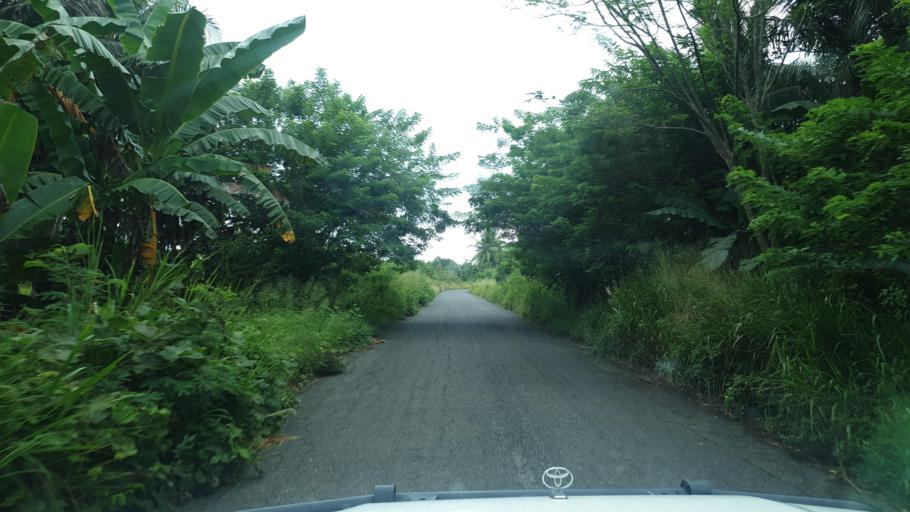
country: PG
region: Gulf
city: Kerema
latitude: -8.1875
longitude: 146.2053
